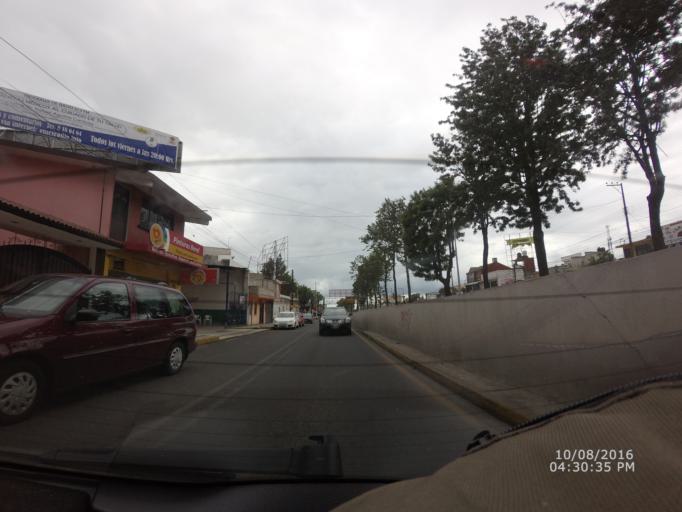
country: MX
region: Veracruz
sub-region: Xalapa
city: Xalapa de Enriquez
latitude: 19.5476
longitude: -96.9110
